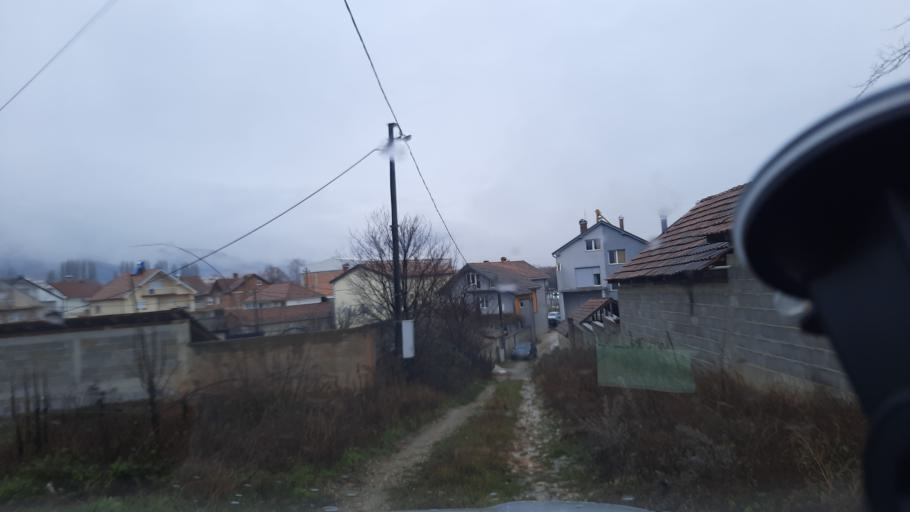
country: MK
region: Opstina Lipkovo
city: Matejche
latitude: 42.1229
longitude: 21.5983
